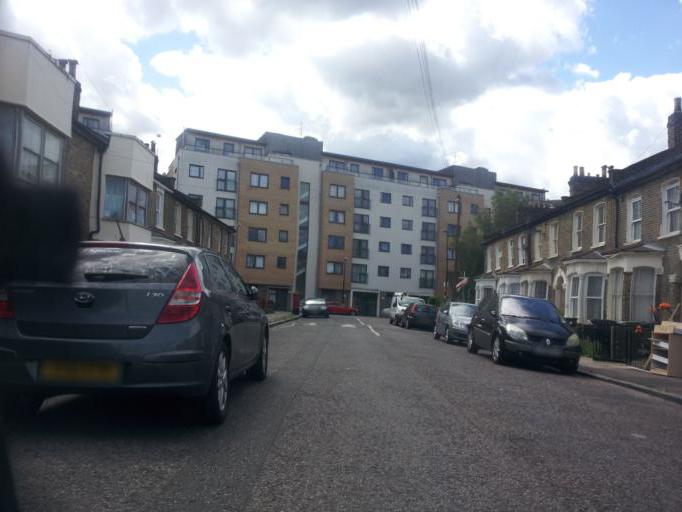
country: GB
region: England
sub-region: Greater London
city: Poplar
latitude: 51.4836
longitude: -0.0365
